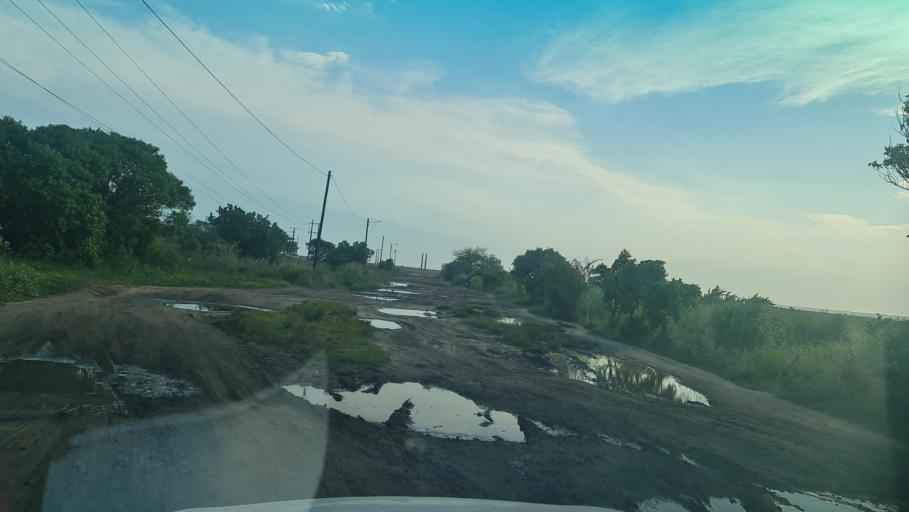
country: MZ
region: Maputo City
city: Maputo
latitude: -25.7371
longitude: 32.7306
